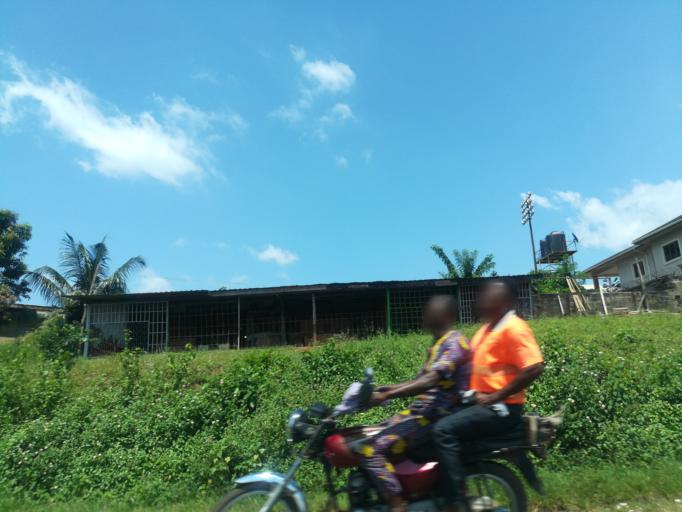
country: NG
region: Oyo
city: Ibadan
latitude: 7.3799
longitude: 3.8619
